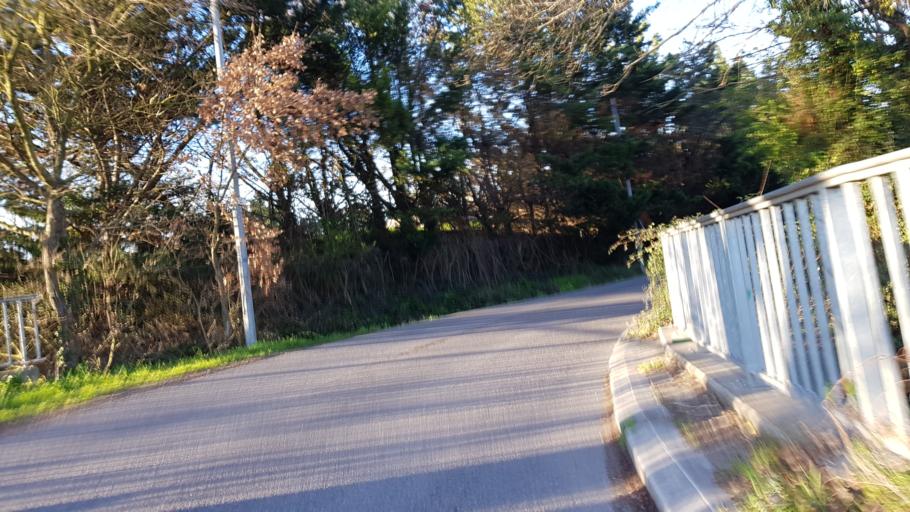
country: FR
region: Provence-Alpes-Cote d'Azur
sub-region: Departement des Bouches-du-Rhone
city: Bouc-Bel-Air
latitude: 43.5003
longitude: 5.4035
